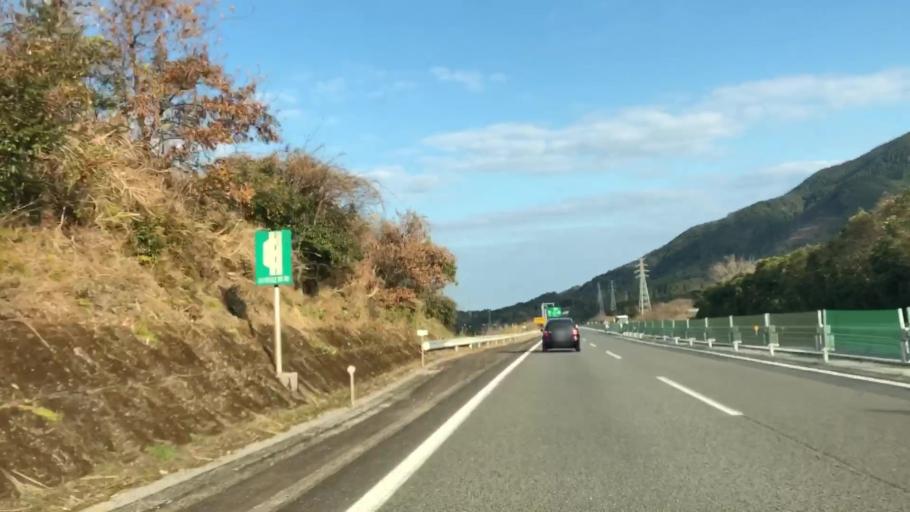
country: JP
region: Miyazaki
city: Miyazaki-shi
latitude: 31.8327
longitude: 131.3262
